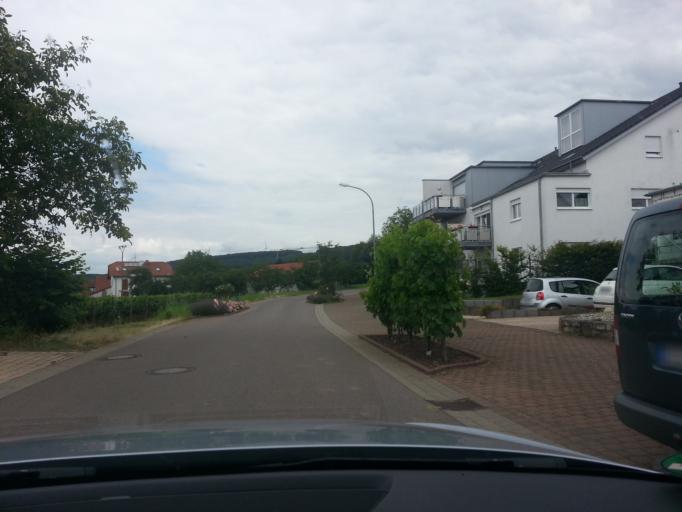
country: DE
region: Saarland
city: Perl
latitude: 49.4694
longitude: 6.3804
